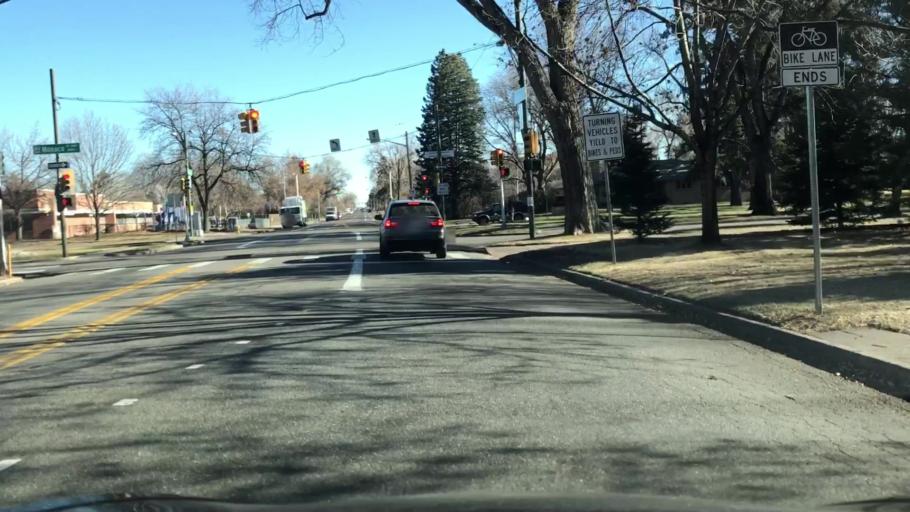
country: US
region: Colorado
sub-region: Arapahoe County
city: Glendale
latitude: 39.7474
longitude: -104.9132
